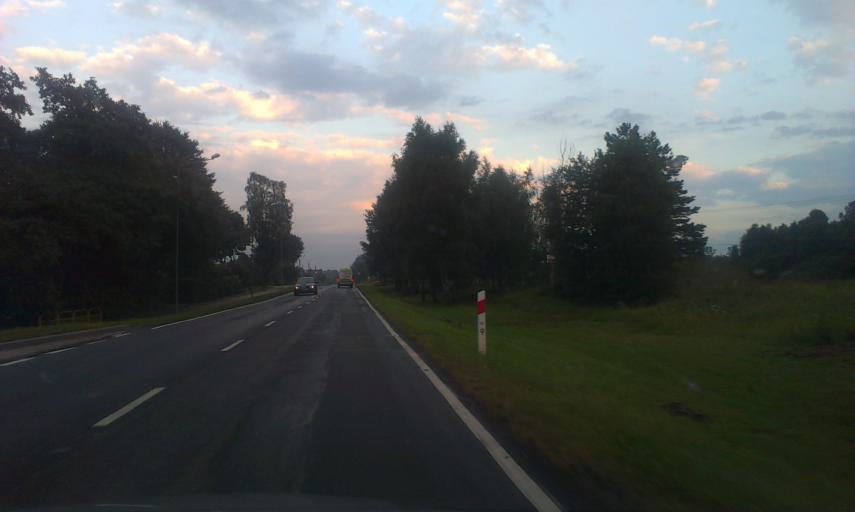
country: PL
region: West Pomeranian Voivodeship
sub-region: Powiat koszalinski
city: Sianow
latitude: 54.1336
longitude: 16.2857
